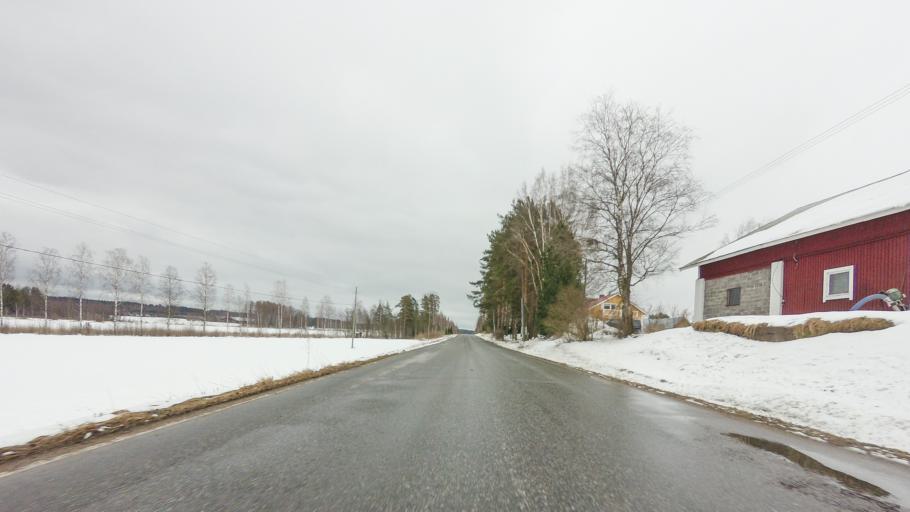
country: FI
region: Southern Savonia
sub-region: Savonlinna
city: Savonlinna
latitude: 61.9587
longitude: 28.8334
